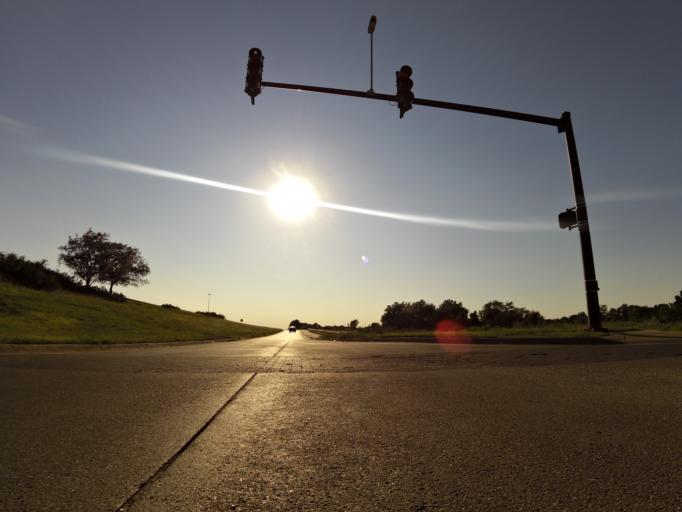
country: US
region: Kansas
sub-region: Sedgwick County
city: Bellaire
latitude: 37.7459
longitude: -97.2624
